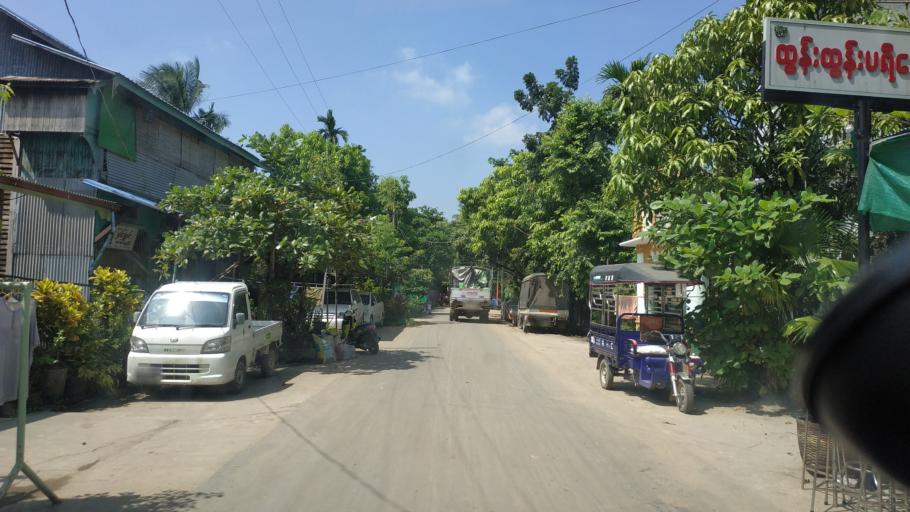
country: MM
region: Ayeyarwady
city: Mawlamyinegyunn
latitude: 16.3782
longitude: 95.2652
